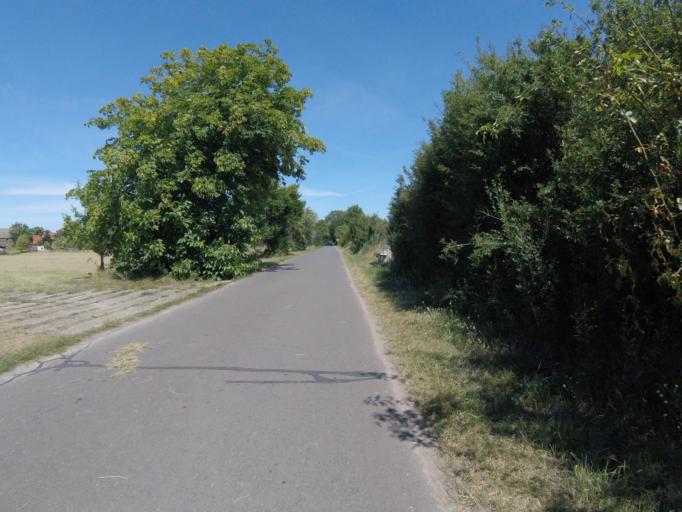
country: DE
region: Brandenburg
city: Mittenwalde
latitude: 52.2831
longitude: 13.5452
